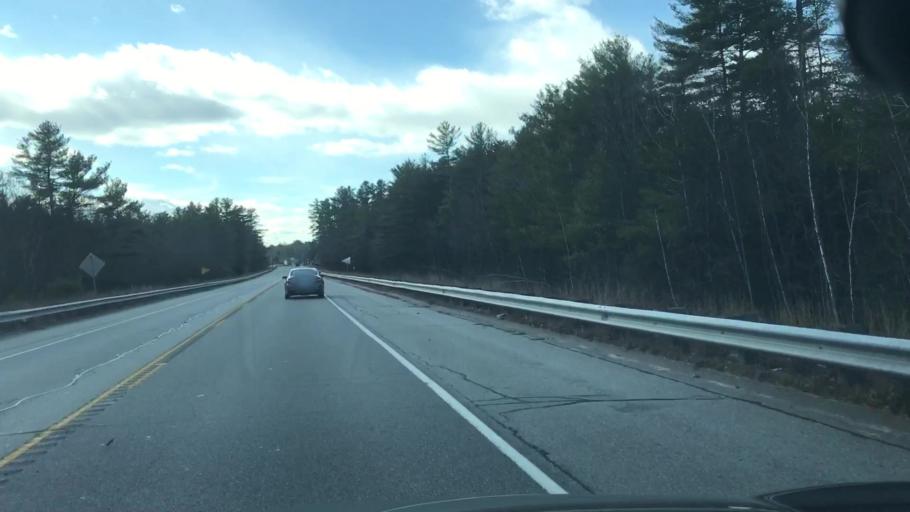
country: US
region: New Hampshire
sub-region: Merrimack County
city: Pittsfield
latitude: 43.3032
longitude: -71.3426
